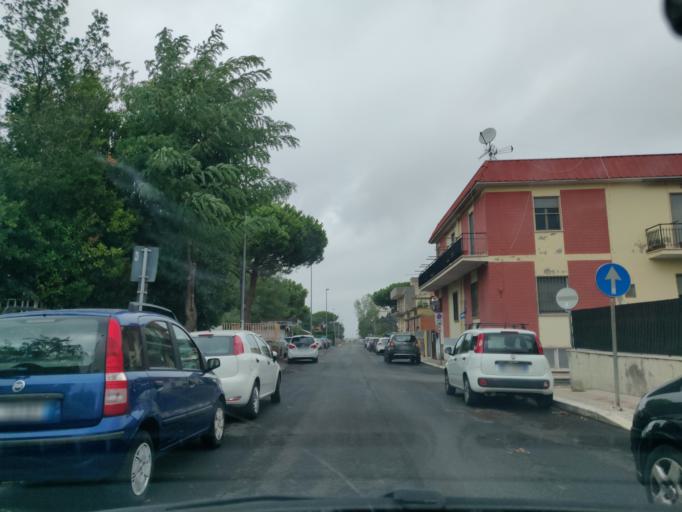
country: IT
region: Latium
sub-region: Citta metropolitana di Roma Capitale
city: Civitavecchia
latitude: 42.1007
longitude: 11.7997
